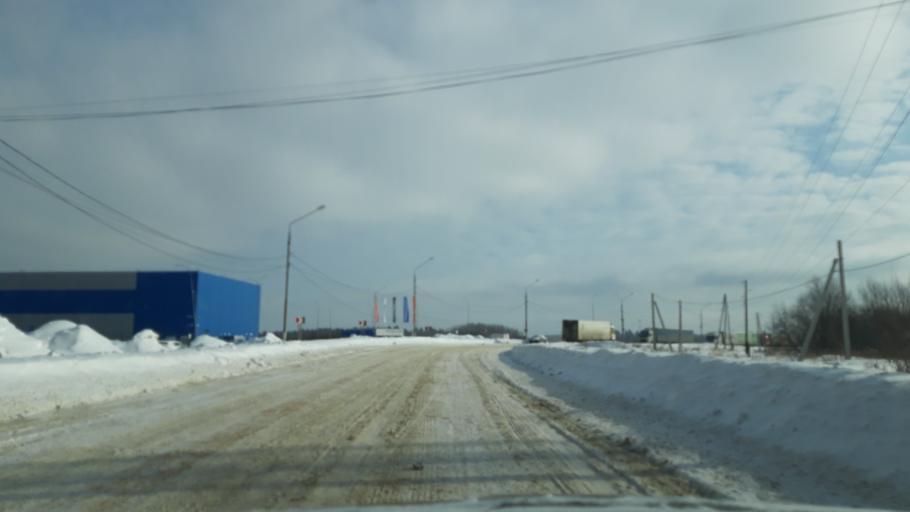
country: RU
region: Moskovskaya
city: Yermolino
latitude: 56.1427
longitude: 37.3786
